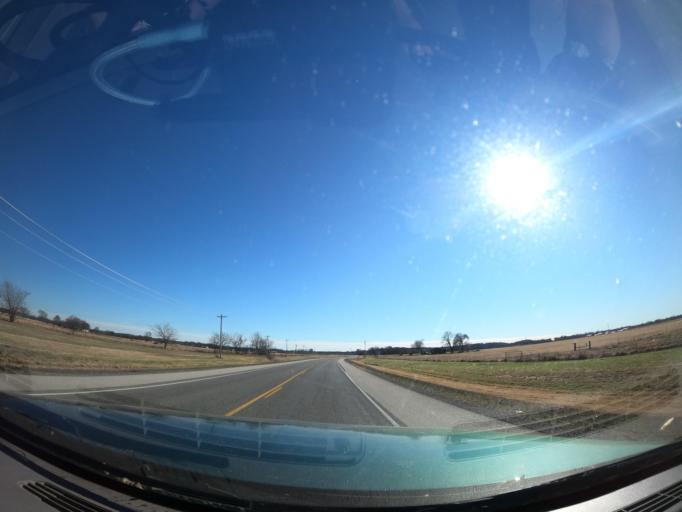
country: US
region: Oklahoma
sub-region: Muskogee County
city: Haskell
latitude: 35.7971
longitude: -95.6694
